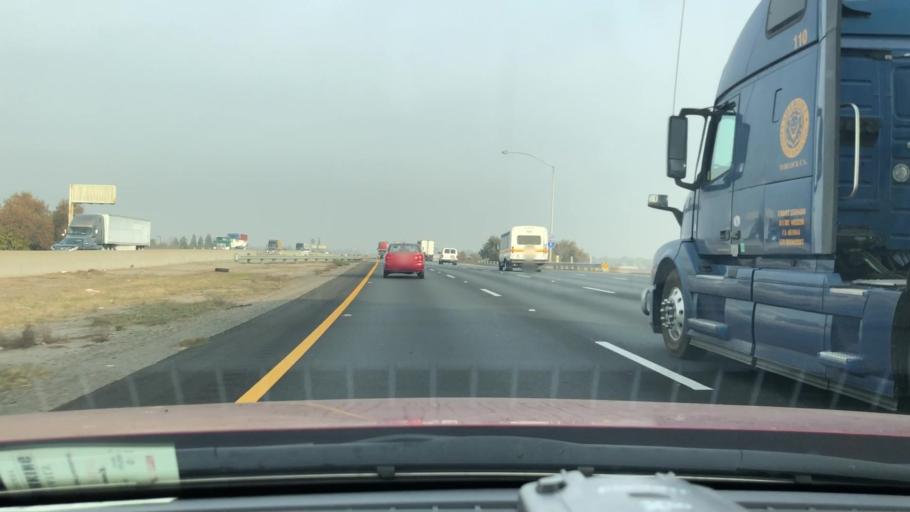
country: US
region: California
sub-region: San Joaquin County
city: French Camp
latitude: 37.8847
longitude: -121.2792
